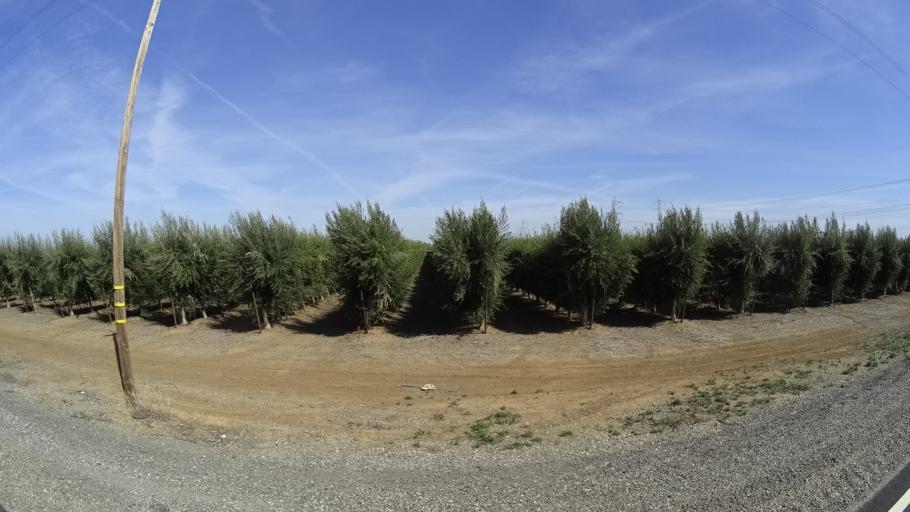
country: US
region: California
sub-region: Glenn County
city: Willows
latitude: 39.5241
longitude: -122.2879
